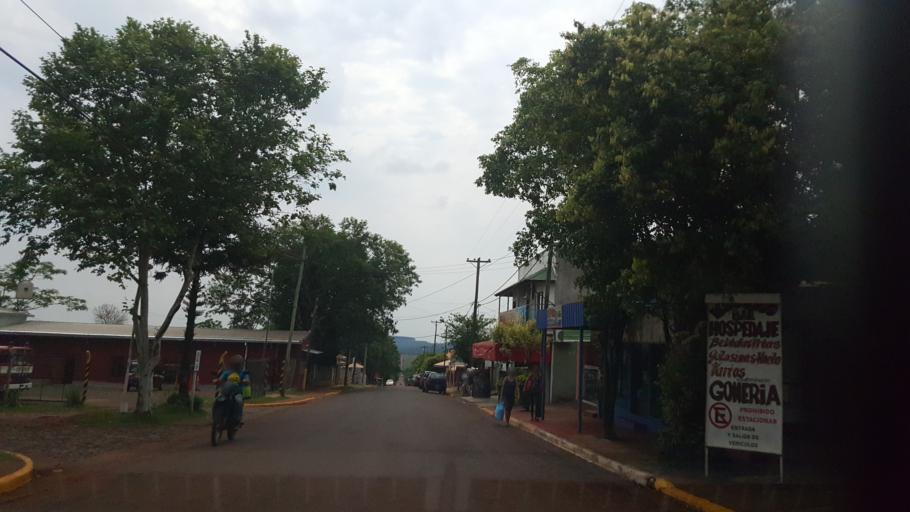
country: AR
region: Misiones
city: Jardin America
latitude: -27.0468
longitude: -55.2438
